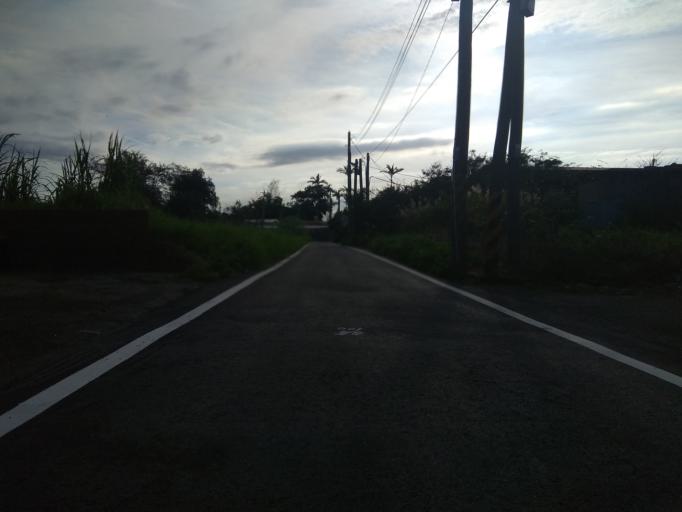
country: TW
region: Taiwan
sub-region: Hsinchu
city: Zhubei
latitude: 24.9409
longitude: 120.9927
